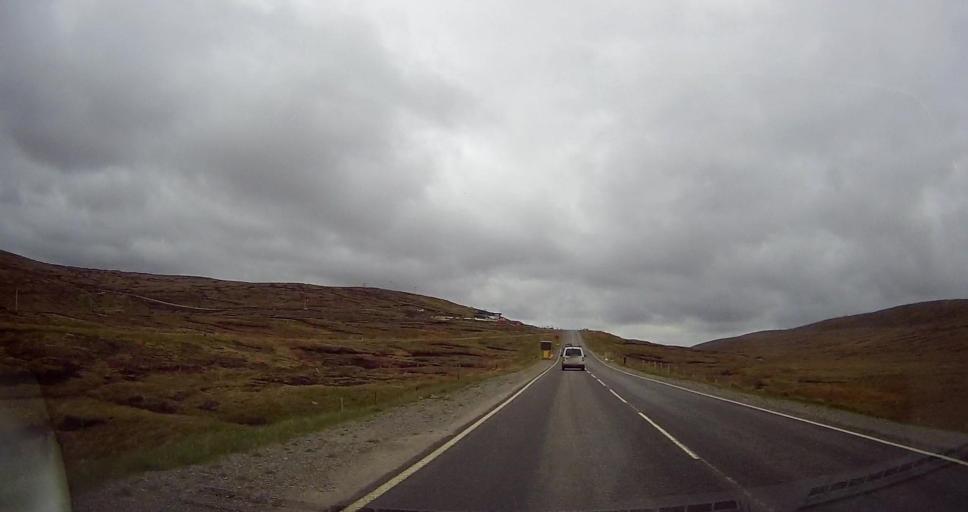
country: GB
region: Scotland
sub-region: Shetland Islands
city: Lerwick
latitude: 60.3290
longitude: -1.2537
